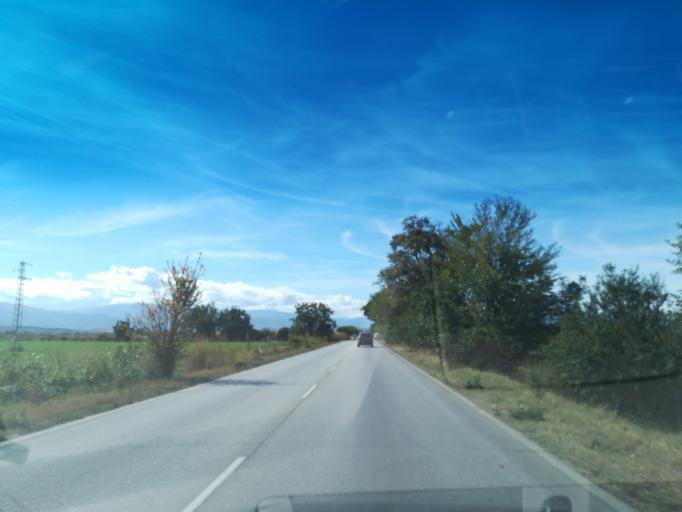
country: BG
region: Plovdiv
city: Stamboliyski
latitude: 42.1244
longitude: 24.5853
